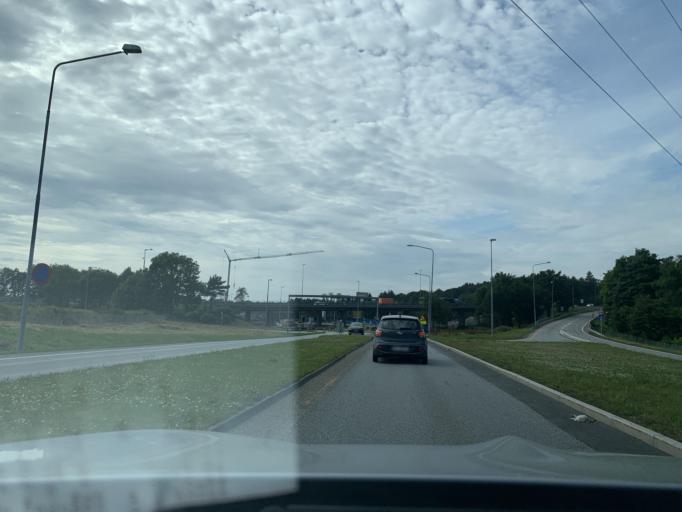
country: NO
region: Rogaland
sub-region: Stavanger
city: Stavanger
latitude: 58.9214
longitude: 5.7091
